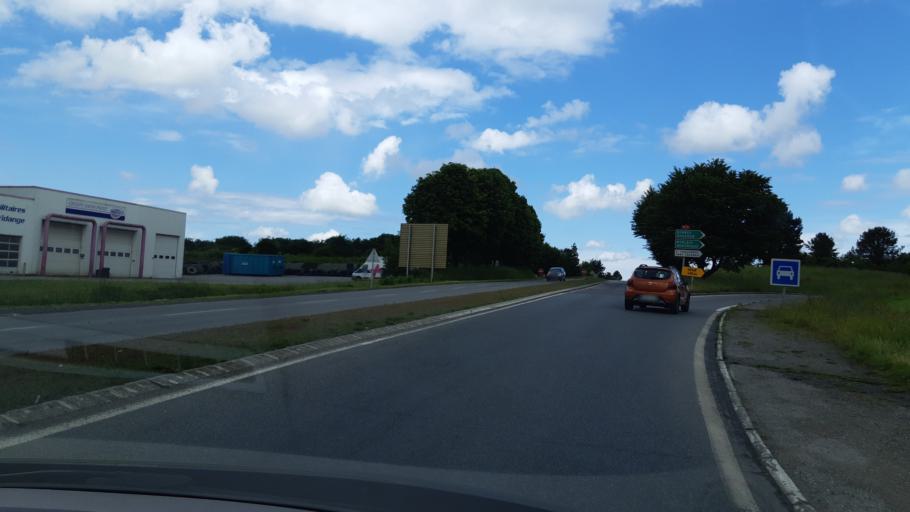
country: FR
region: Brittany
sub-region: Departement du Finistere
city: Landivisiau
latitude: 48.5159
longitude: -4.0539
